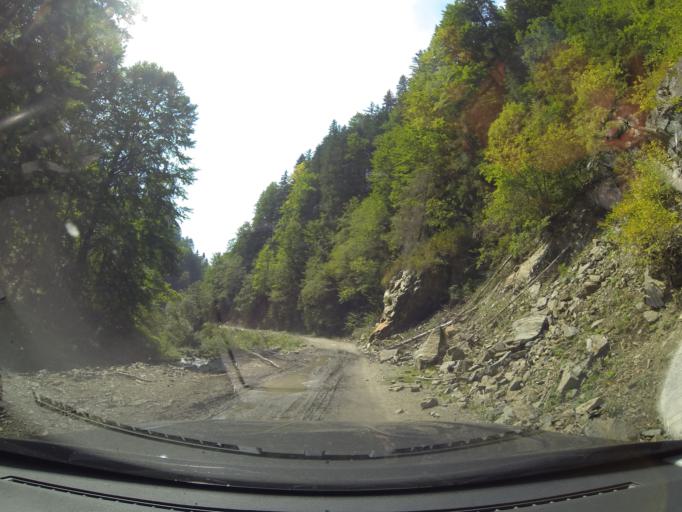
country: RO
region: Arges
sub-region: Comuna Arefu
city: Arefu
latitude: 45.5027
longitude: 24.6565
